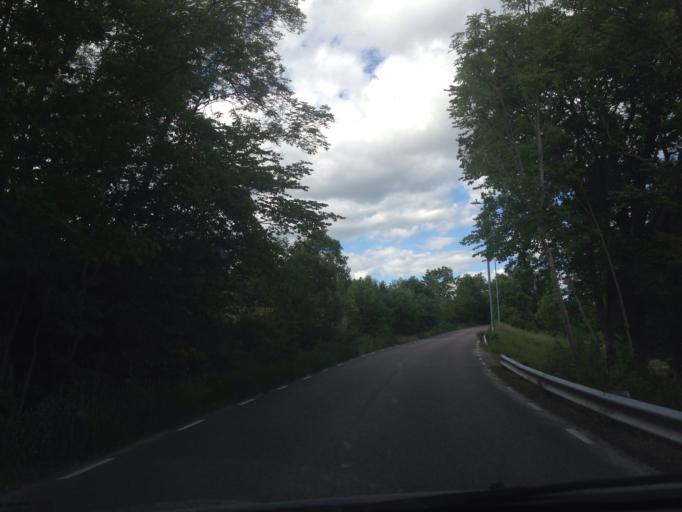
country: SE
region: Vaestra Goetaland
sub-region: Goteborg
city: Goeteborg
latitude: 57.7783
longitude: 11.9330
